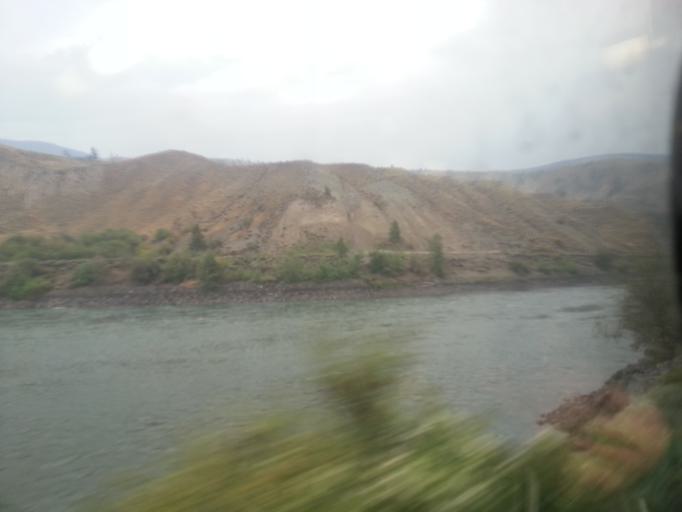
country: CA
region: British Columbia
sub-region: Thompson-Nicola Regional District
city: Ashcroft
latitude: 50.5068
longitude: -121.2856
